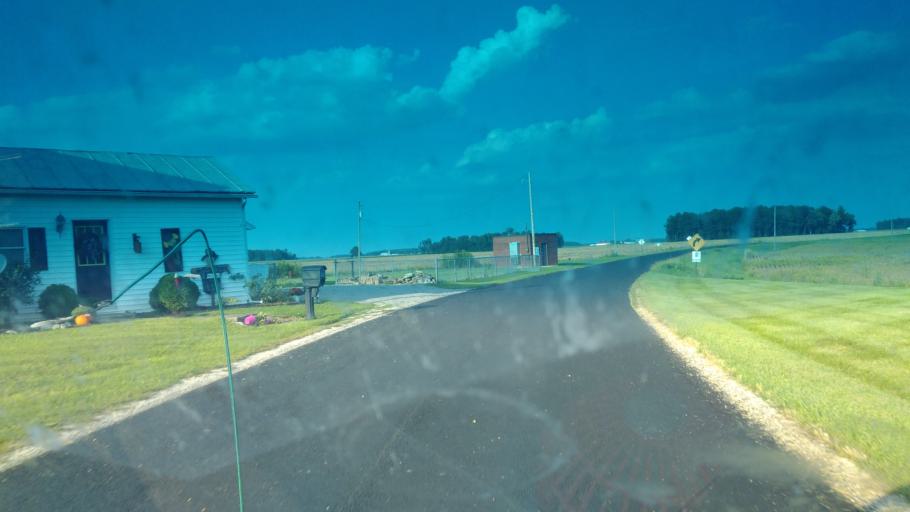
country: US
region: Ohio
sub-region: Crawford County
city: Bucyrus
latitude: 40.9652
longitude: -83.0153
